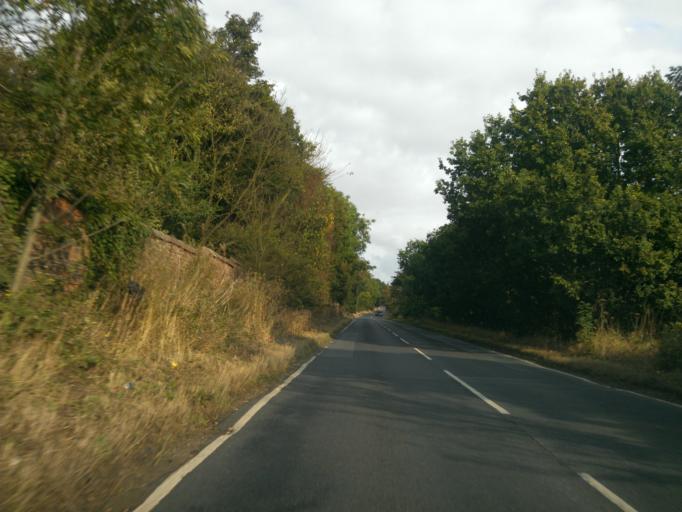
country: GB
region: England
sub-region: Essex
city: Great Totham
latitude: 51.8003
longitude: 0.6966
